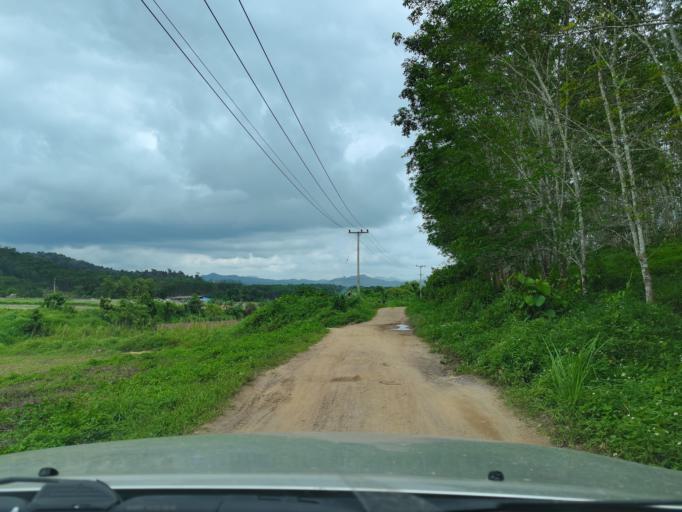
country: LA
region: Loungnamtha
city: Muang Long
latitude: 20.6979
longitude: 101.0377
